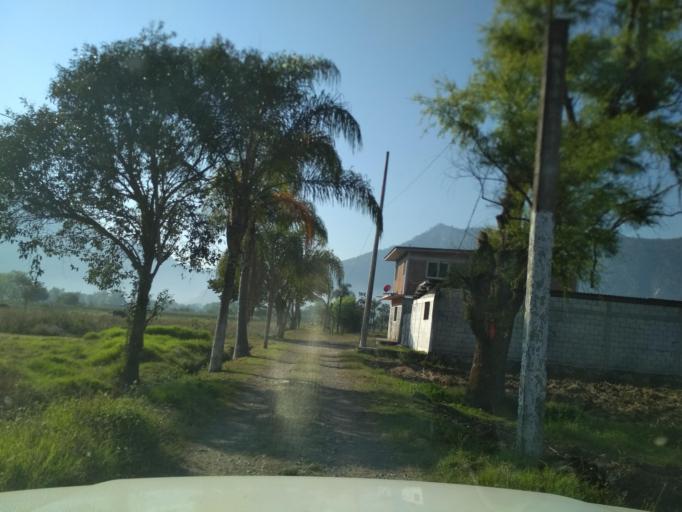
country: MX
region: Veracruz
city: Jalapilla
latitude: 18.8245
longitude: -97.0781
